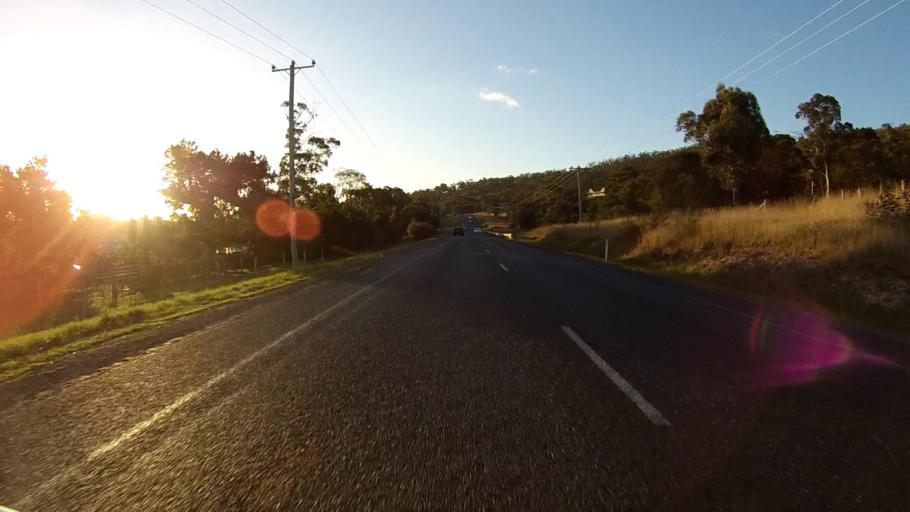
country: AU
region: Tasmania
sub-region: Sorell
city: Sorell
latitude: -42.7905
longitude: 147.6067
